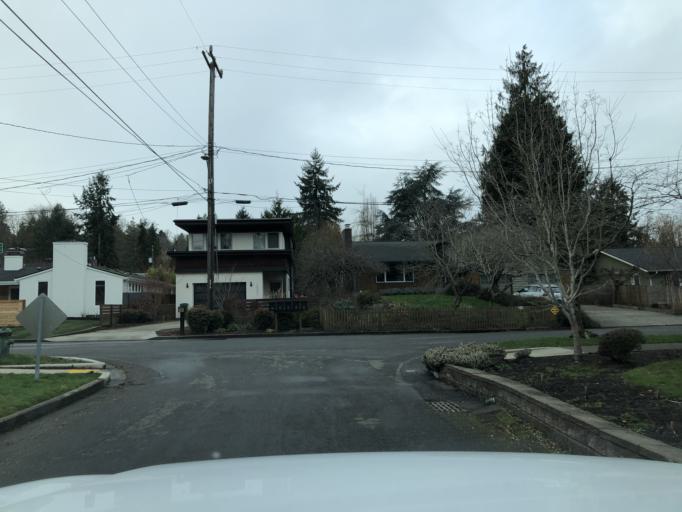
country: US
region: Washington
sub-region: King County
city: Lake Forest Park
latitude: 47.7038
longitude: -122.2852
